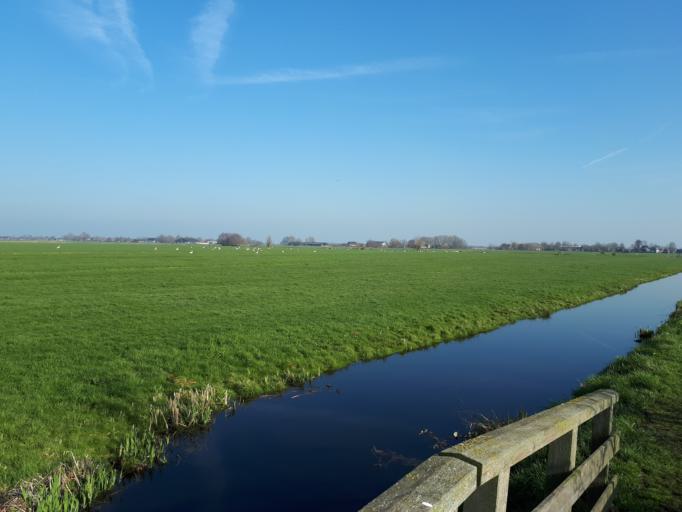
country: NL
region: South Holland
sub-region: Gemeente Gouda
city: Gouda
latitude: 51.9575
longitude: 4.7114
